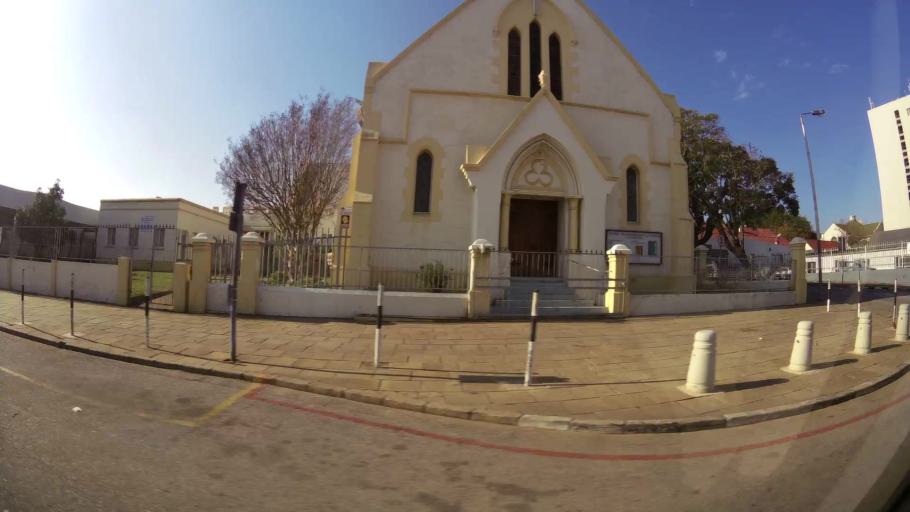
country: ZA
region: Eastern Cape
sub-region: Nelson Mandela Bay Metropolitan Municipality
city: Uitenhage
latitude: -33.7652
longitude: 25.3977
